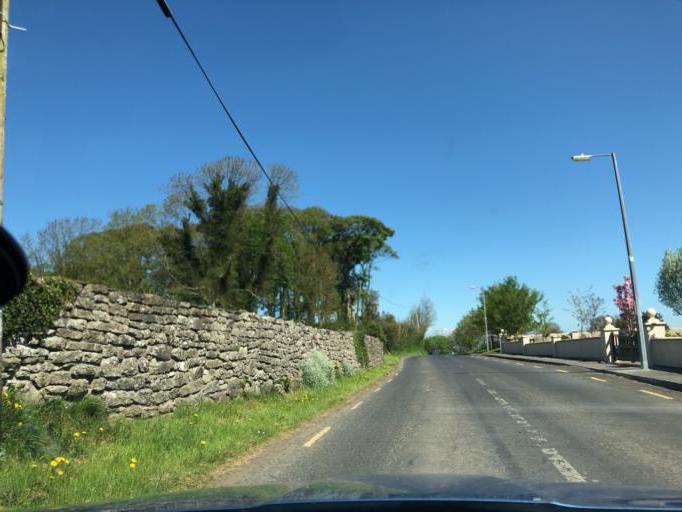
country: IE
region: Connaught
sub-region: County Galway
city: Portumna
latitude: 53.1402
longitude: -8.3670
